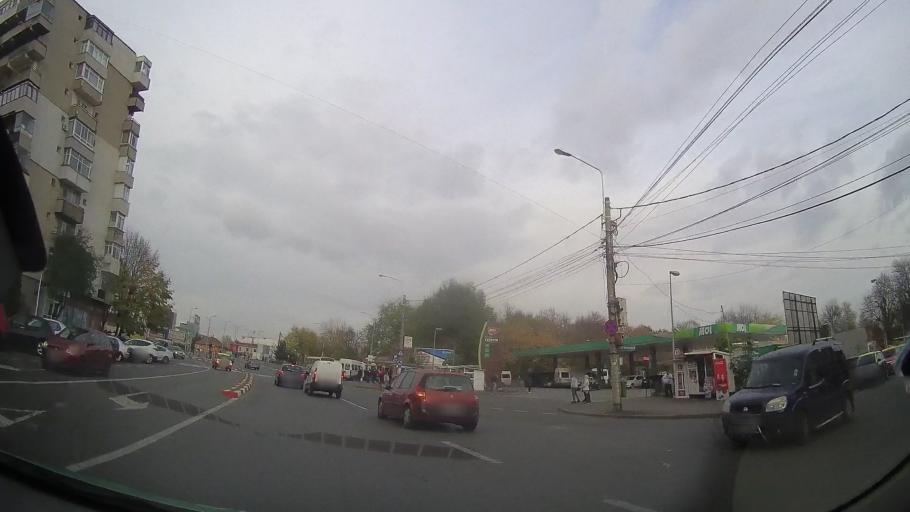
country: RO
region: Prahova
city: Ploiesti
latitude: 44.9449
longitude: 26.0348
